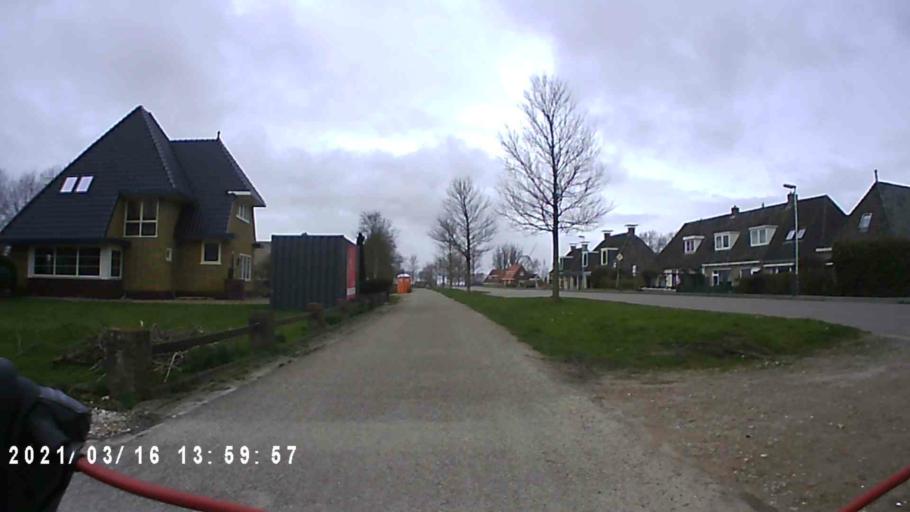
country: NL
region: Friesland
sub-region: Gemeente Franekeradeel
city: Sexbierum
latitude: 53.1842
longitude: 5.4948
